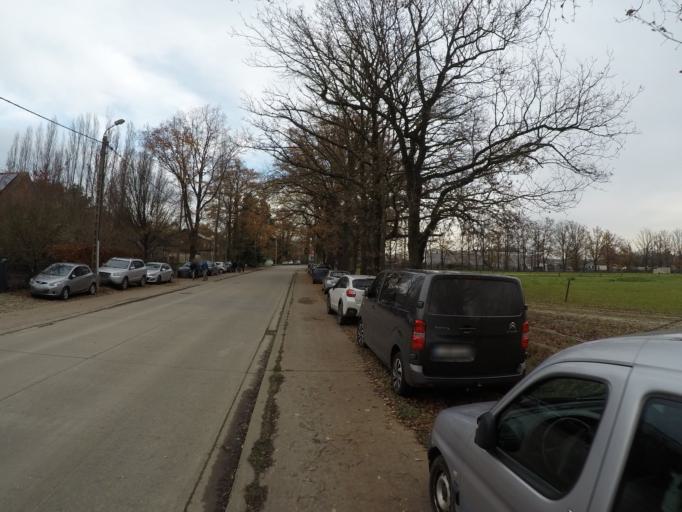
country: BE
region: Flanders
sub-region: Provincie Antwerpen
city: Hulshout
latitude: 51.0810
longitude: 4.8006
